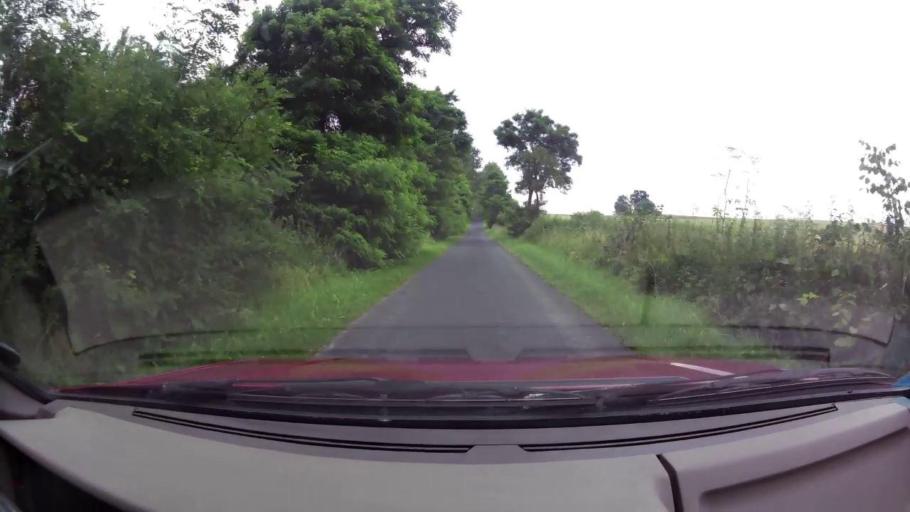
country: PL
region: West Pomeranian Voivodeship
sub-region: Powiat drawski
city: Drawsko Pomorskie
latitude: 53.5227
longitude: 15.7560
